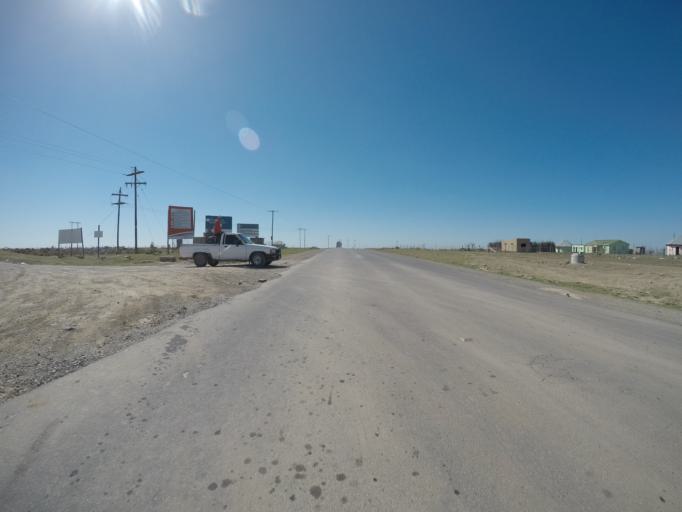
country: ZA
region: Eastern Cape
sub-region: OR Tambo District Municipality
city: Mthatha
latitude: -31.8944
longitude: 28.7828
